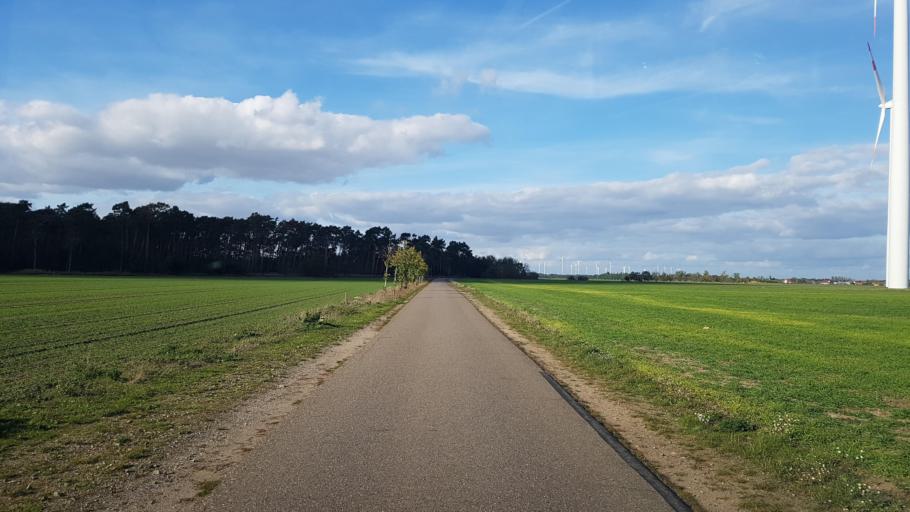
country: DE
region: Brandenburg
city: Bad Liebenwerda
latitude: 51.4716
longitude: 13.3287
